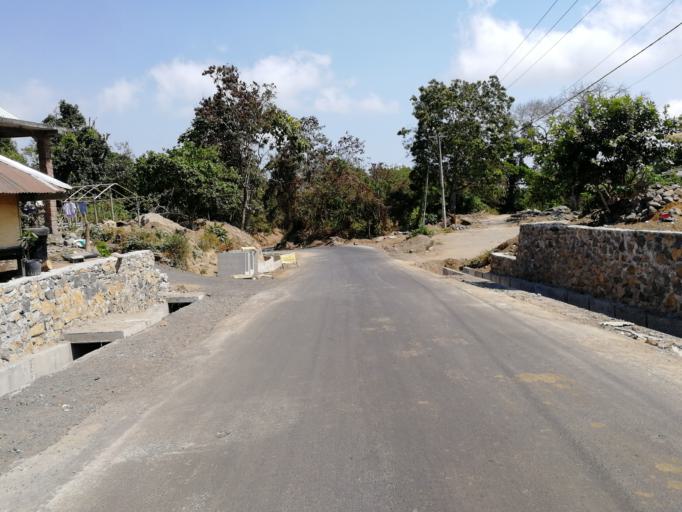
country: ID
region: West Nusa Tenggara
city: Lelongken
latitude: -8.3318
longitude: 116.4976
